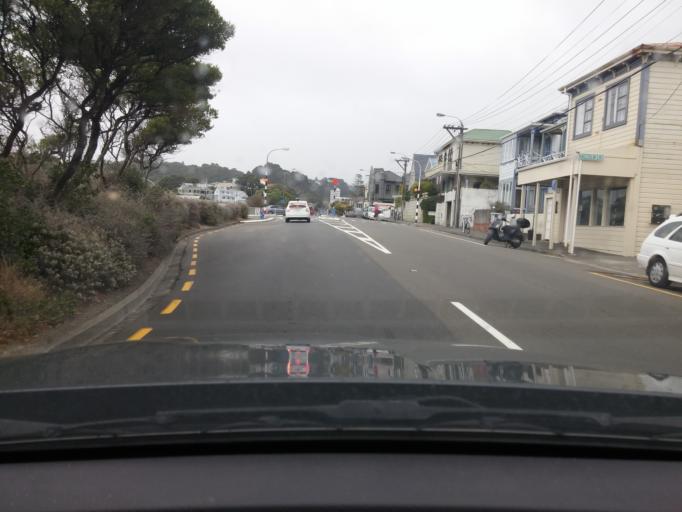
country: NZ
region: Wellington
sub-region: Wellington City
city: Kelburn
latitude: -41.2742
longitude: 174.7747
